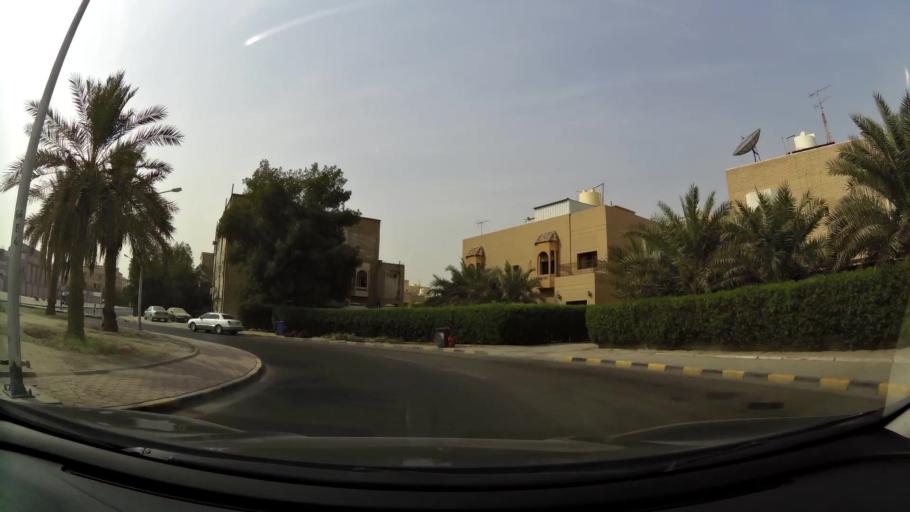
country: KW
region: Al Farwaniyah
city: Al Farwaniyah
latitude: 29.2838
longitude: 47.9442
